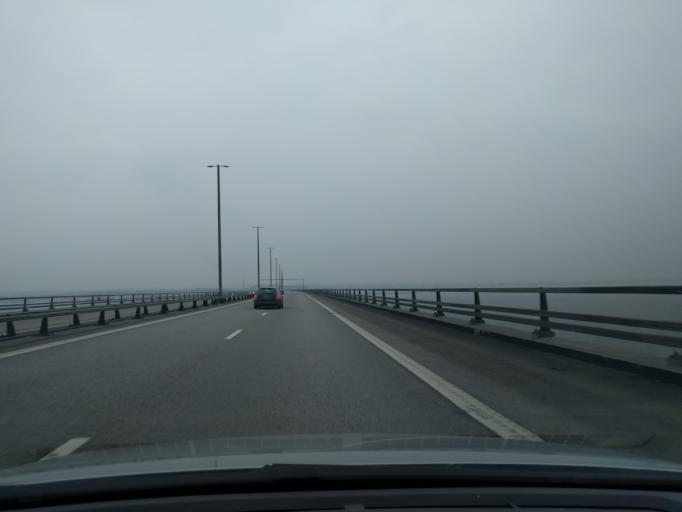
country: SE
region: Skane
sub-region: Malmo
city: Bunkeflostrand
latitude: 55.5668
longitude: 12.8714
